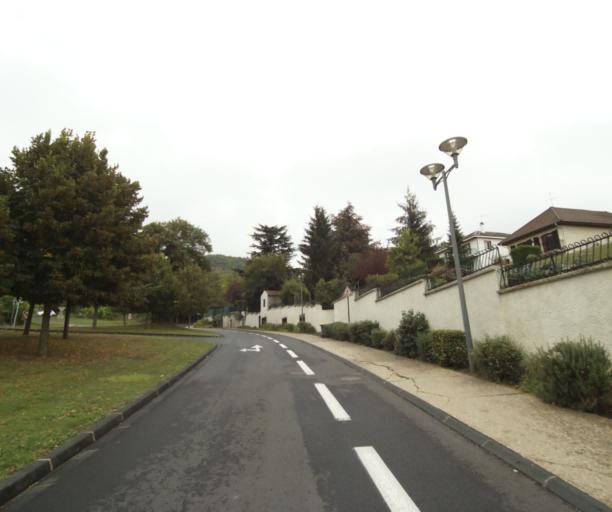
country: FR
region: Auvergne
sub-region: Departement du Puy-de-Dome
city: Romagnat
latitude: 45.7261
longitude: 3.1011
